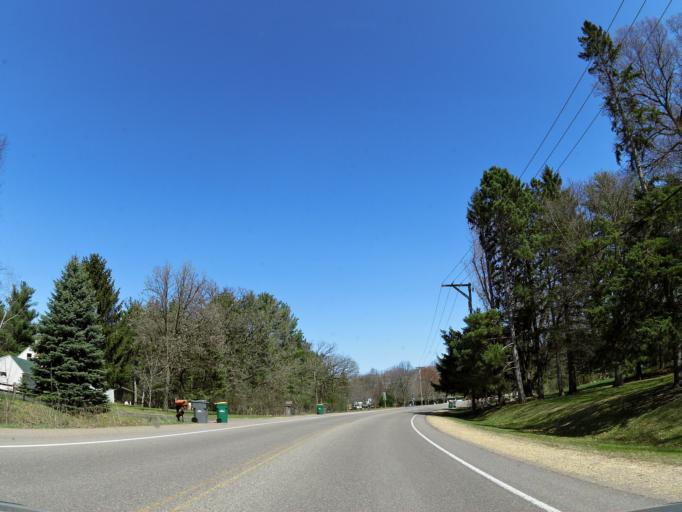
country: US
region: Wisconsin
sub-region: Saint Croix County
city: North Hudson
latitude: 44.9880
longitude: -92.7303
